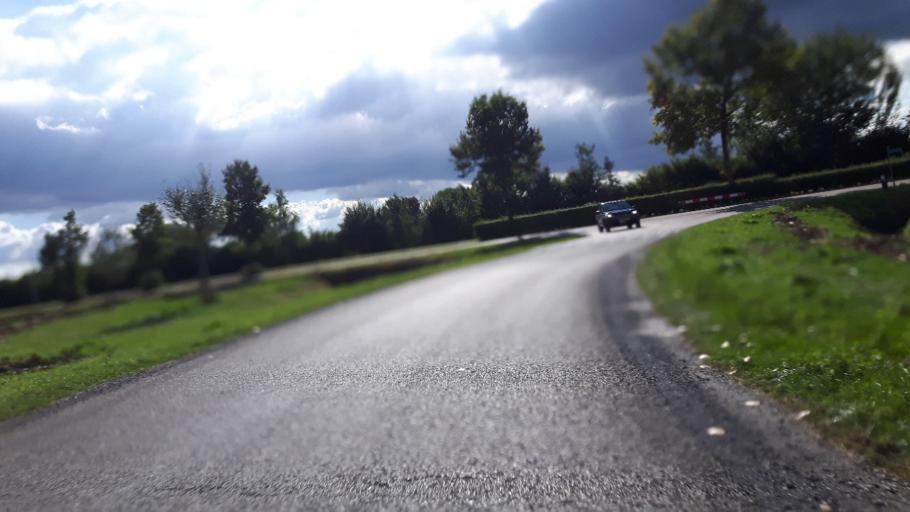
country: NL
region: South Holland
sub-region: Gemeente Leerdam
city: Leerdam
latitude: 51.8871
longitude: 5.1319
